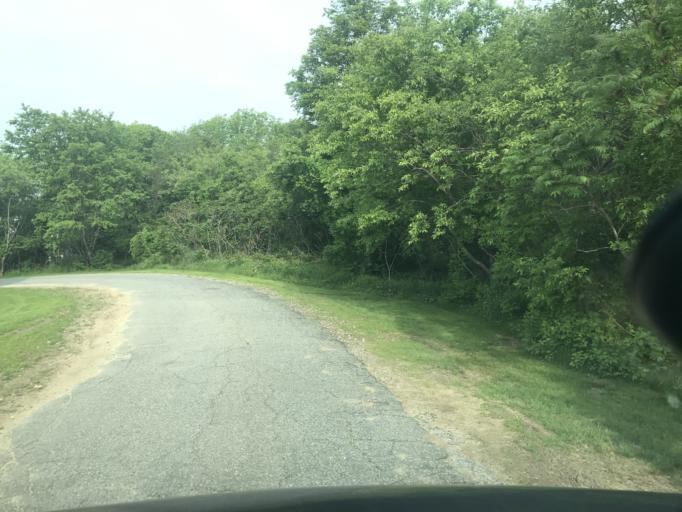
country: US
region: Massachusetts
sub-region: Essex County
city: Rockport
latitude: 42.6724
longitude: -70.6289
